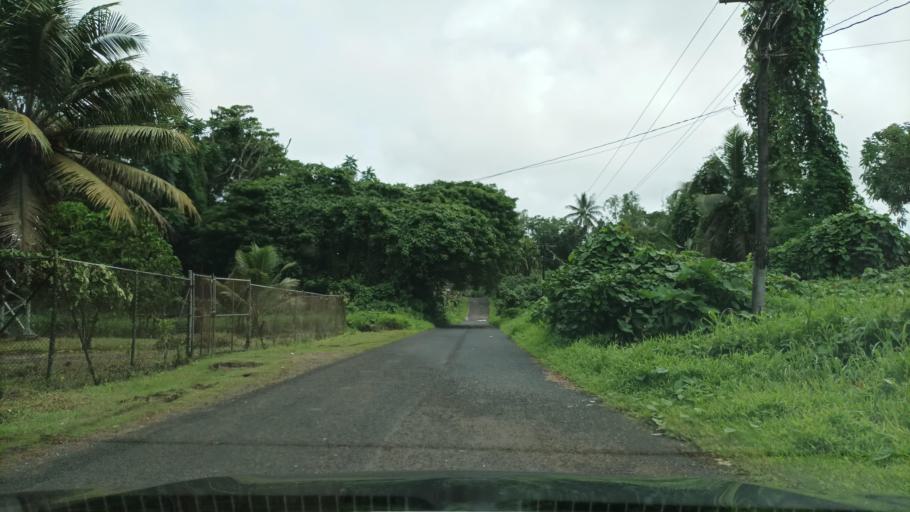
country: FM
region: Pohnpei
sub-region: Madolenihm Municipality
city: Madolenihm Municipality Government
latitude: 6.8374
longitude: 158.2986
